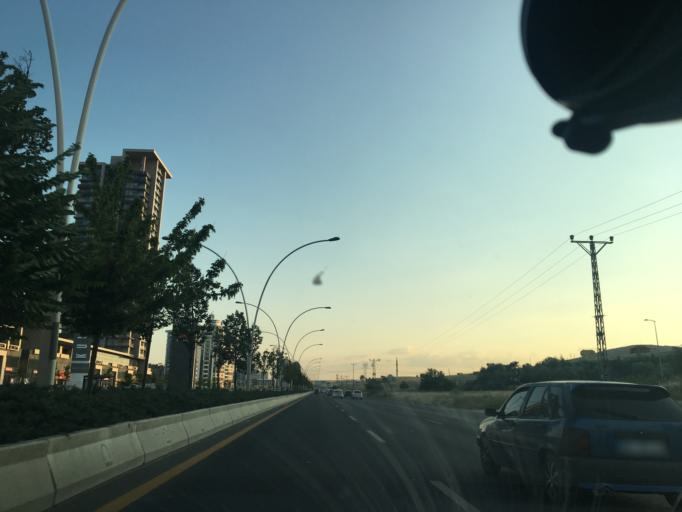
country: TR
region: Ankara
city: Etimesgut
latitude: 39.8761
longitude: 32.6509
